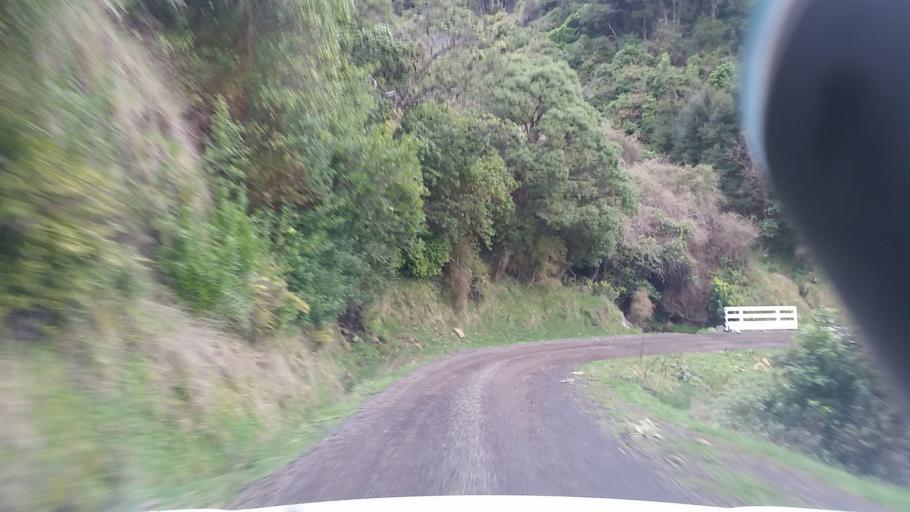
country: NZ
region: Canterbury
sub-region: Christchurch City
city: Christchurch
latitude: -43.8204
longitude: 172.9891
